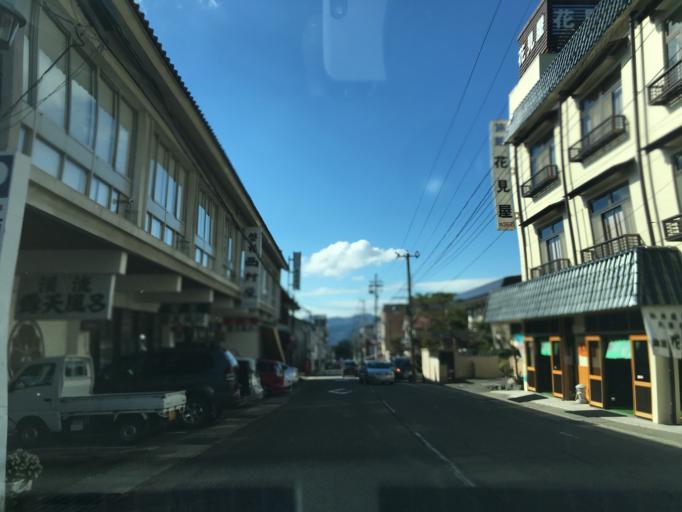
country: JP
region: Fukushima
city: Inawashiro
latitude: 37.6144
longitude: 140.2111
